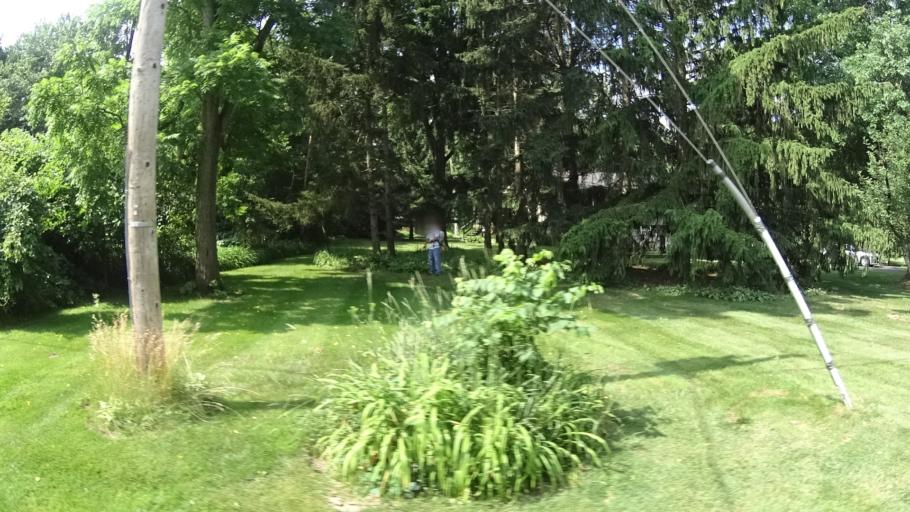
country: US
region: Ohio
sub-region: Lorain County
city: Vermilion
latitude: 41.3731
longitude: -82.3931
